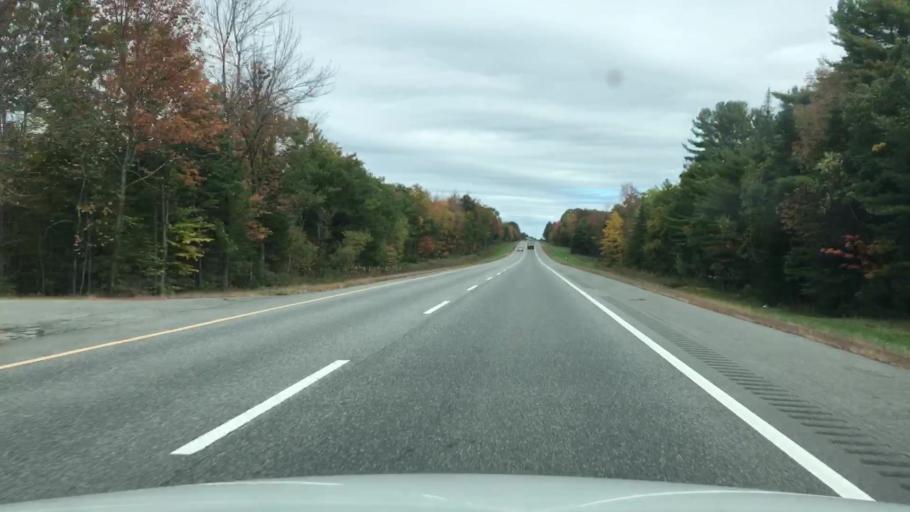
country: US
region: Maine
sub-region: Kennebec County
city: Sidney
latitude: 44.4119
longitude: -69.7461
